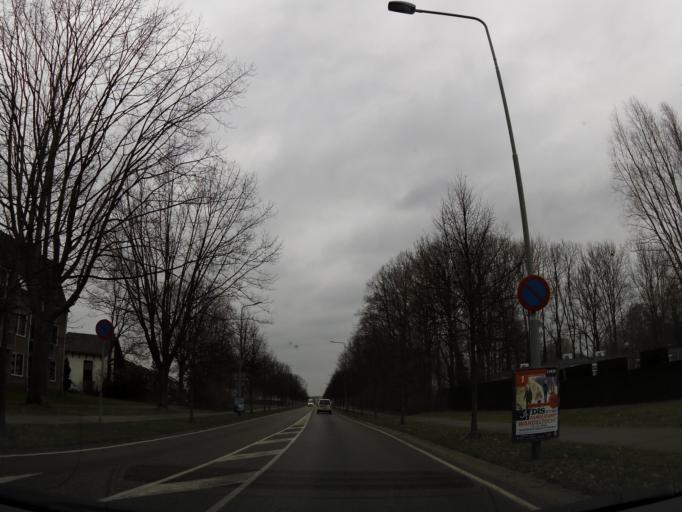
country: NL
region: Limburg
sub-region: Gemeente Sittard-Geleen
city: Sittard
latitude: 51.0100
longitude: 5.8743
